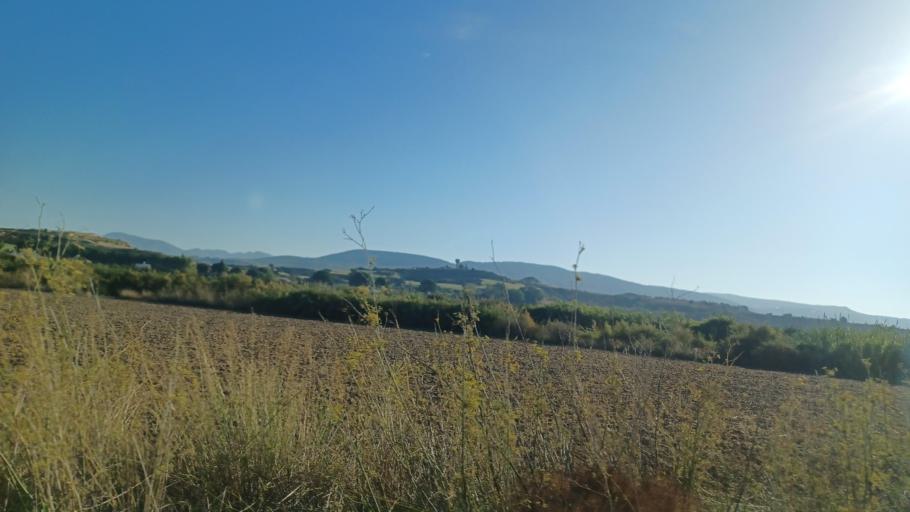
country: CY
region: Pafos
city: Polis
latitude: 35.0138
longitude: 32.4292
